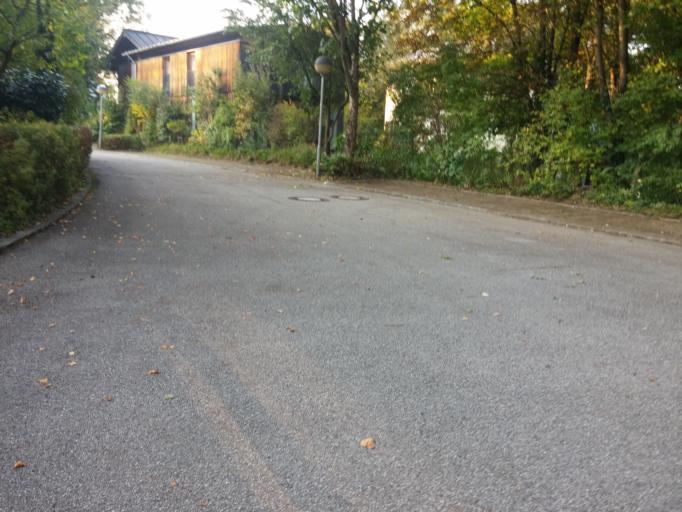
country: DE
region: Bavaria
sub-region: Upper Bavaria
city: Zorneding
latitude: 48.0913
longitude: 11.8307
